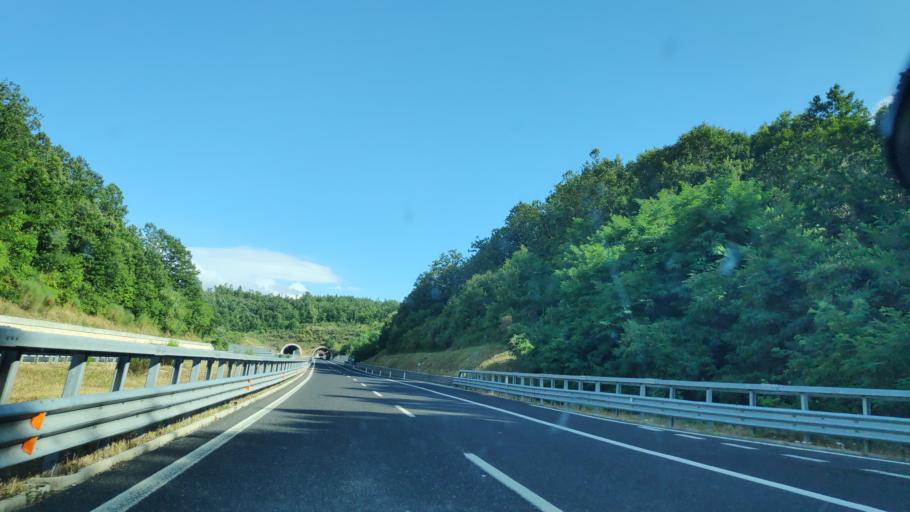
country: IT
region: Campania
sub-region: Provincia di Salerno
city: Casalbuono
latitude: 40.2371
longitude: 15.6611
